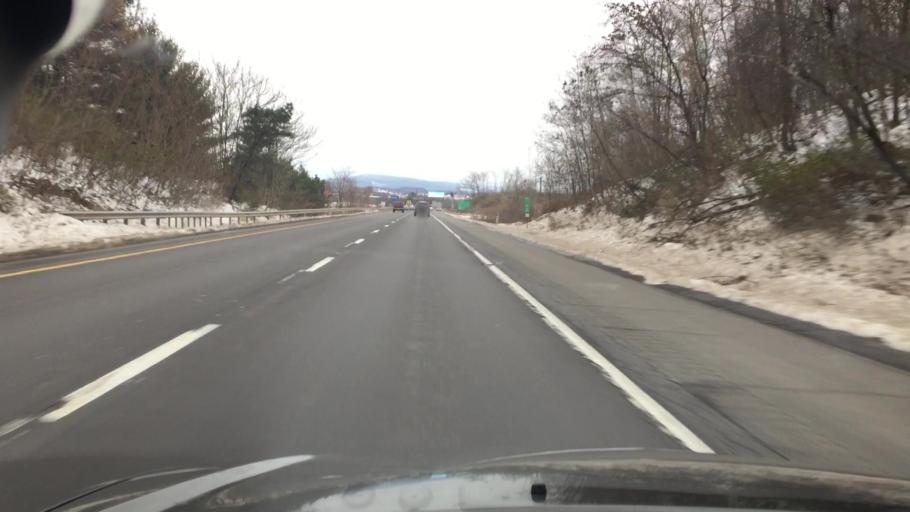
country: US
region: Pennsylvania
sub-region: Luzerne County
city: Ashley
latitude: 41.2173
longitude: -75.8838
